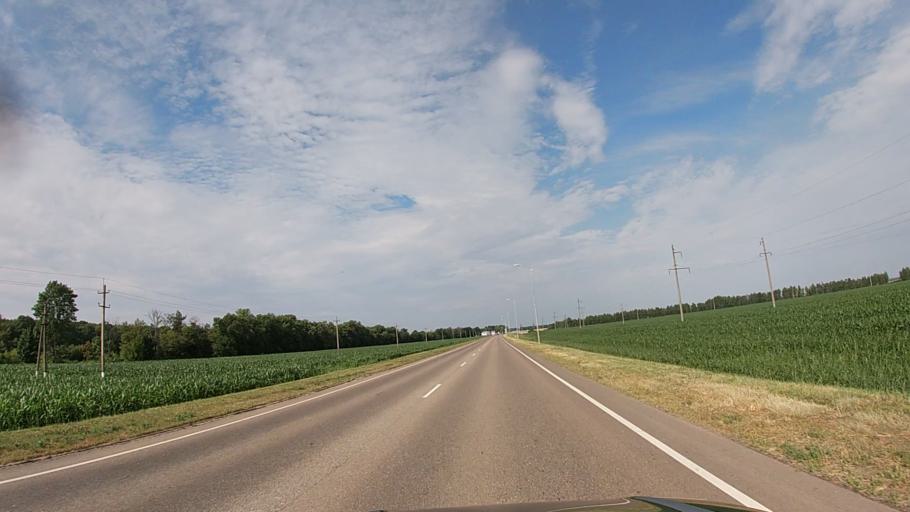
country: RU
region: Belgorod
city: Proletarskiy
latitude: 50.7999
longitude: 35.7252
